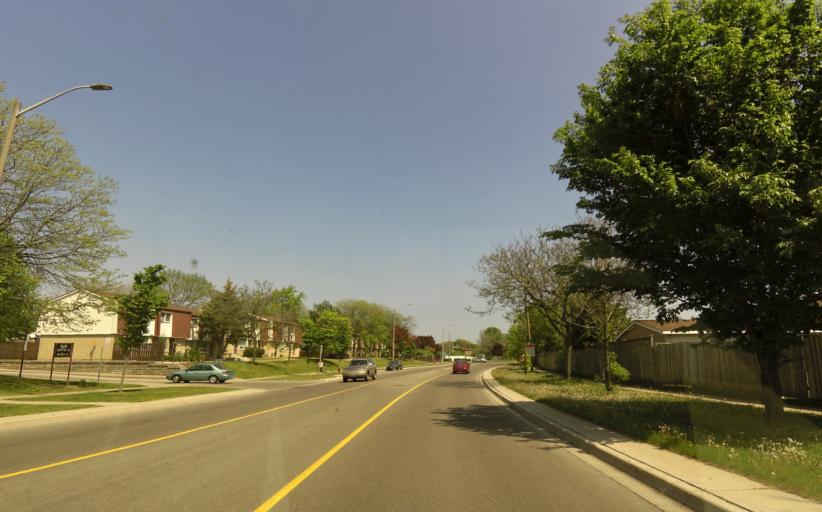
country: CA
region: Ontario
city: Mississauga
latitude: 43.5915
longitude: -79.6156
